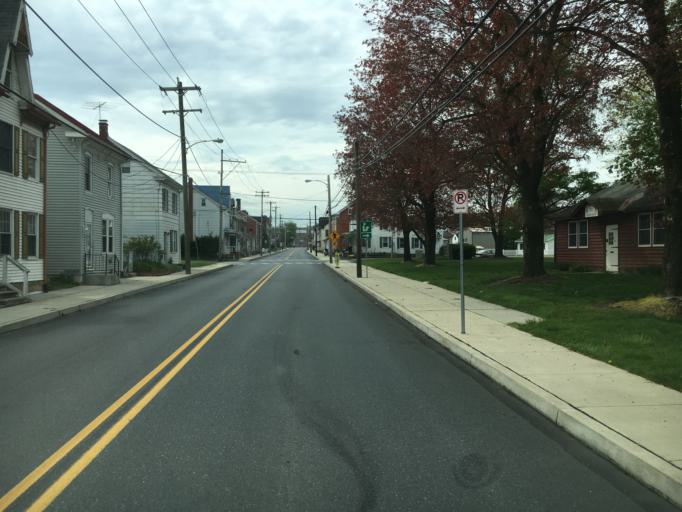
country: US
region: Pennsylvania
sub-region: Berks County
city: Fleetwood
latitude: 40.4570
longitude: -75.8192
